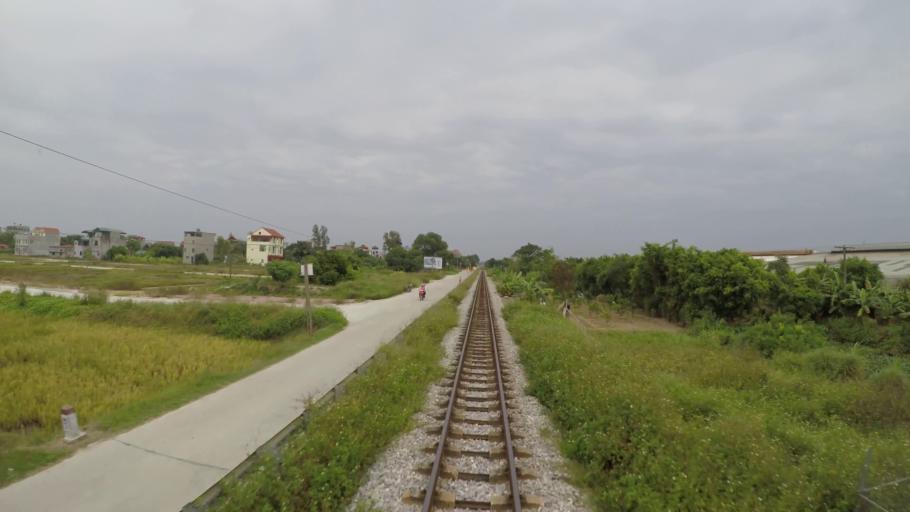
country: VN
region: Hai Duong
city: Lai Cach
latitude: 20.9520
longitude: 106.2337
